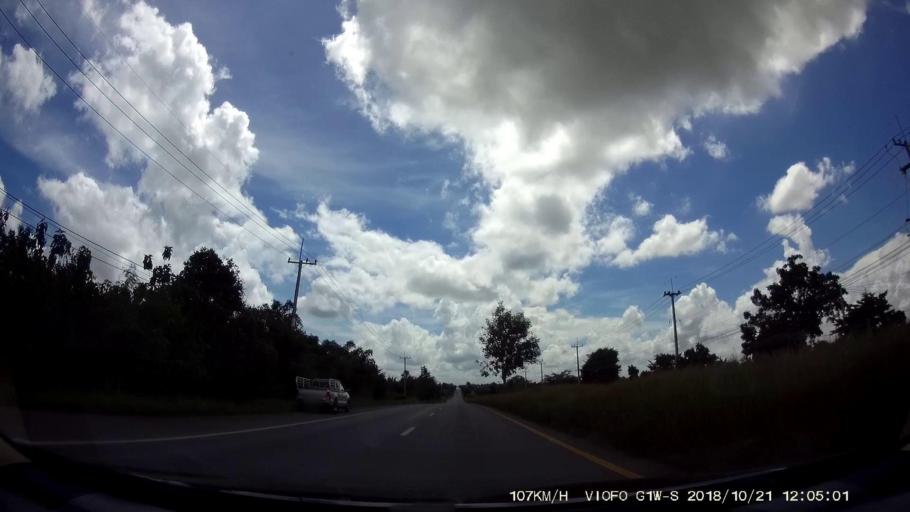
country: TH
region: Chaiyaphum
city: Chatturat
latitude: 15.4854
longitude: 101.8225
